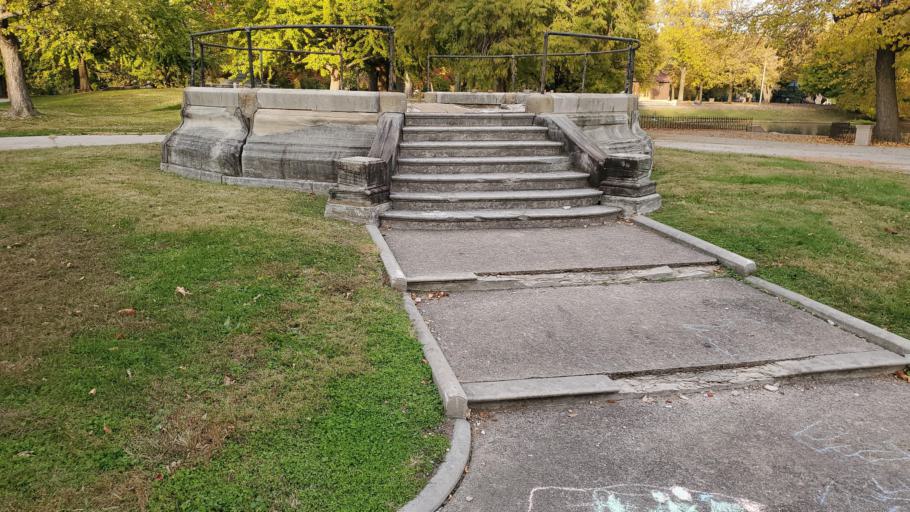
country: US
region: Missouri
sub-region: City of Saint Louis
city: St. Louis
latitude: 38.6155
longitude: -90.2168
